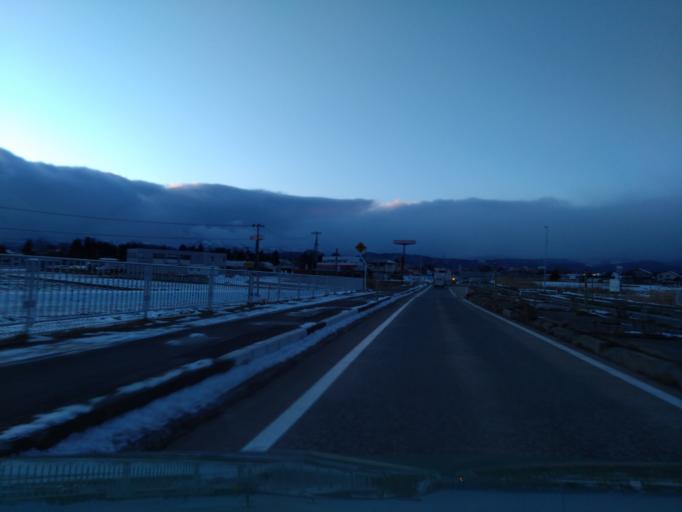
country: JP
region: Iwate
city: Shizukuishi
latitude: 39.6918
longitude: 140.9845
